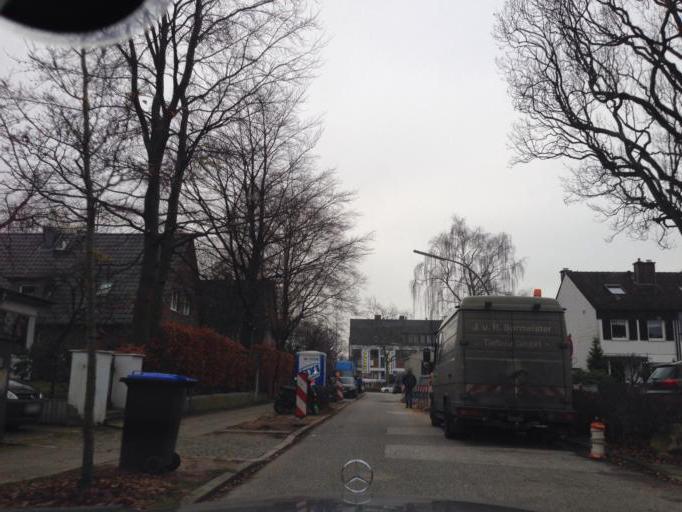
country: DE
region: Hamburg
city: Wandsbek
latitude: 53.5771
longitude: 10.0989
